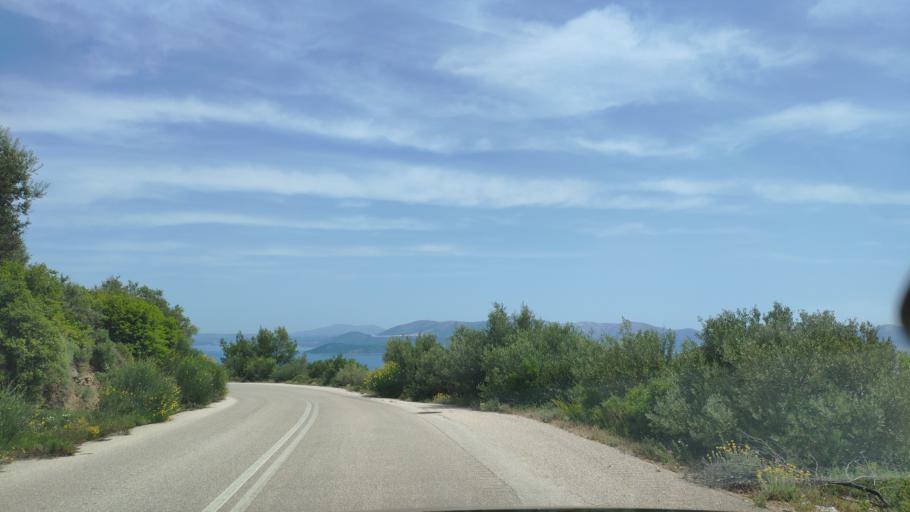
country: GR
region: Attica
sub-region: Nomarchia Anatolikis Attikis
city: Grammatiko
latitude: 38.2527
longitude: 23.9688
